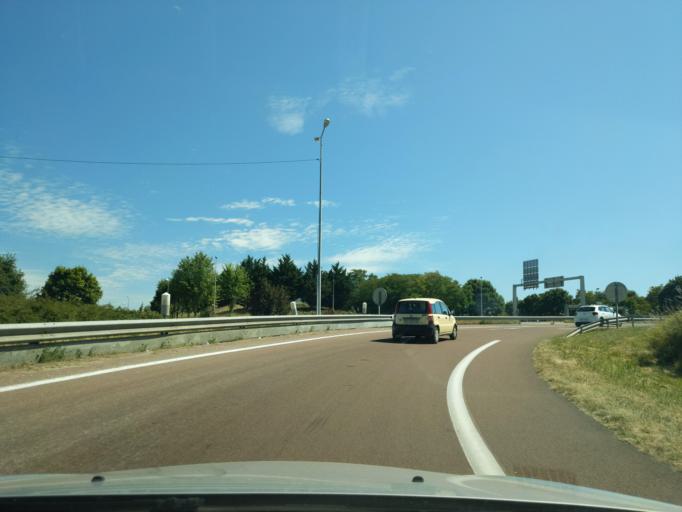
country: FR
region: Bourgogne
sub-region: Departement de la Cote-d'Or
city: Longvic
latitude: 47.3030
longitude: 5.0746
